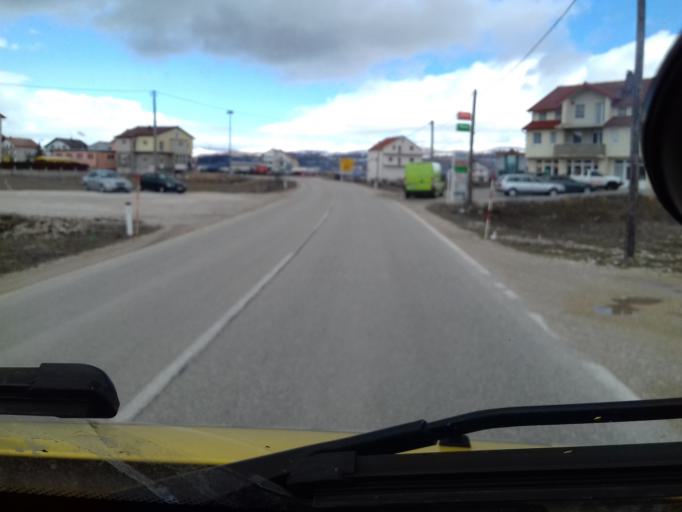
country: BA
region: Federation of Bosnia and Herzegovina
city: Tomislavgrad
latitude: 43.7120
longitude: 17.2389
